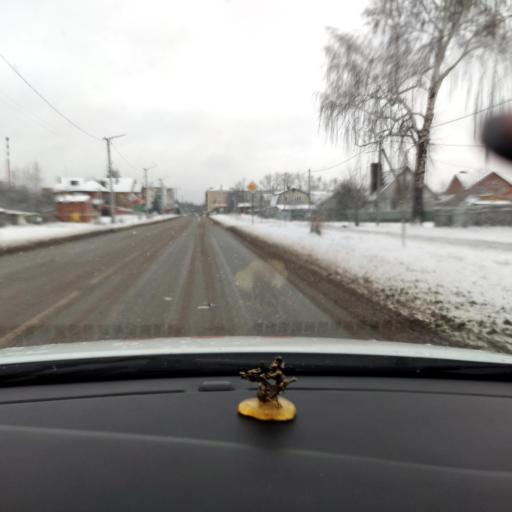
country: RU
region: Tatarstan
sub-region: Zelenodol'skiy Rayon
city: Zelenodolsk
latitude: 55.8535
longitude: 48.5305
